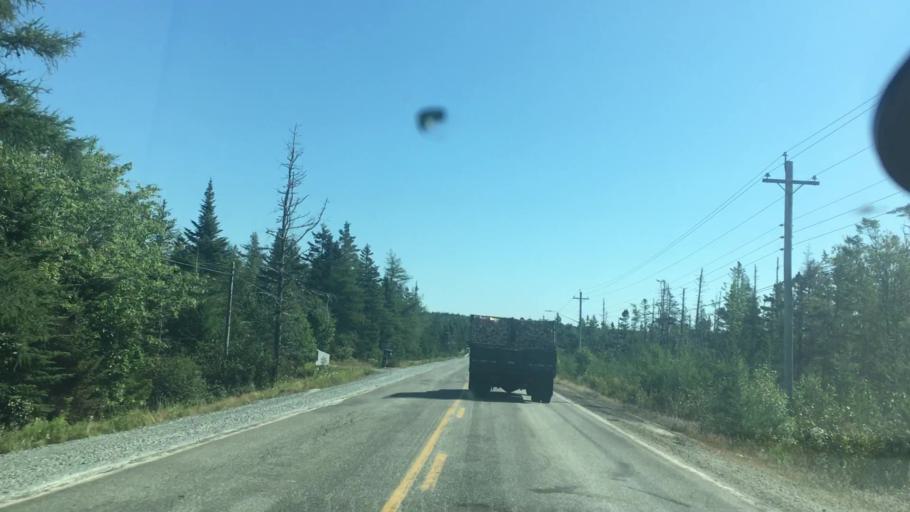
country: CA
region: Nova Scotia
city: New Glasgow
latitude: 44.9034
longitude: -62.4570
